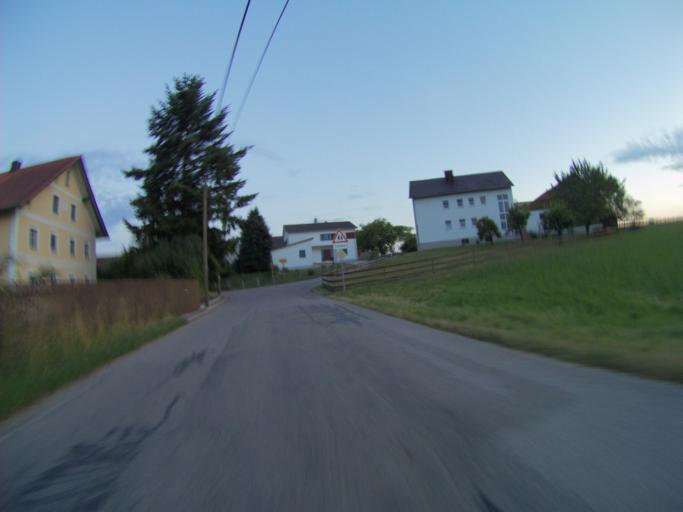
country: DE
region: Bavaria
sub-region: Upper Bavaria
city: Marzling
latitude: 48.4285
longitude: 11.7820
